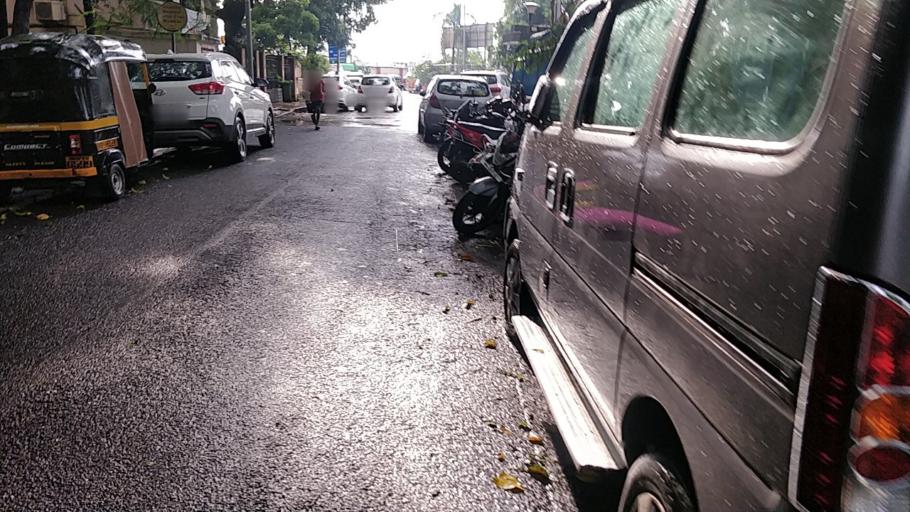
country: IN
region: Maharashtra
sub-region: Mumbai Suburban
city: Mumbai
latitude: 19.0980
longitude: 72.8402
